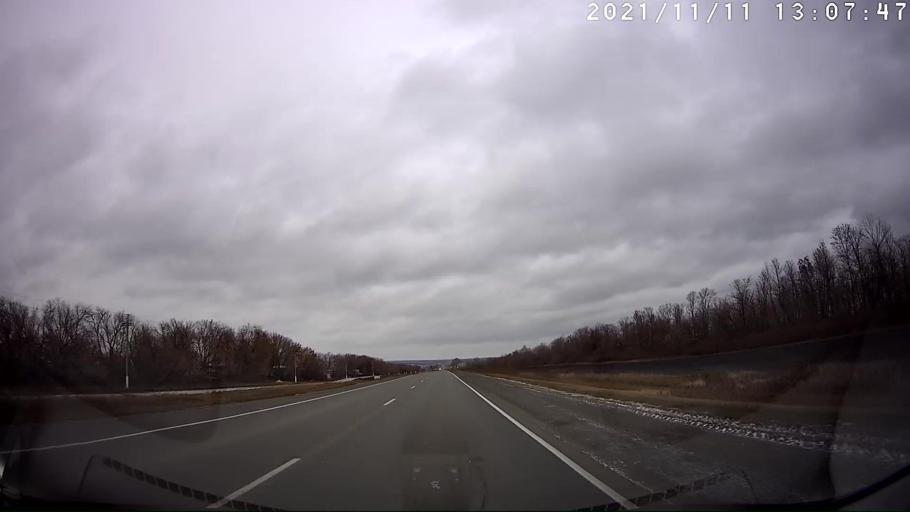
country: RU
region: Chuvashia
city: Batyrevo
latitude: 55.0350
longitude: 47.5691
